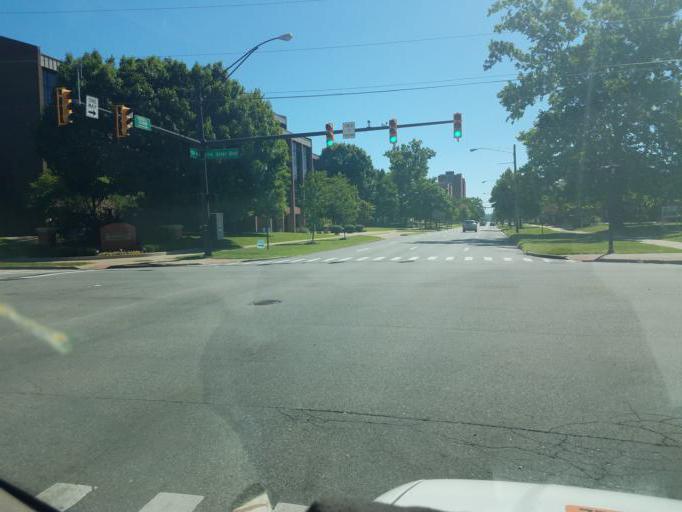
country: US
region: West Virginia
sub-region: Cabell County
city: Huntington
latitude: 38.4214
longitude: -82.4316
